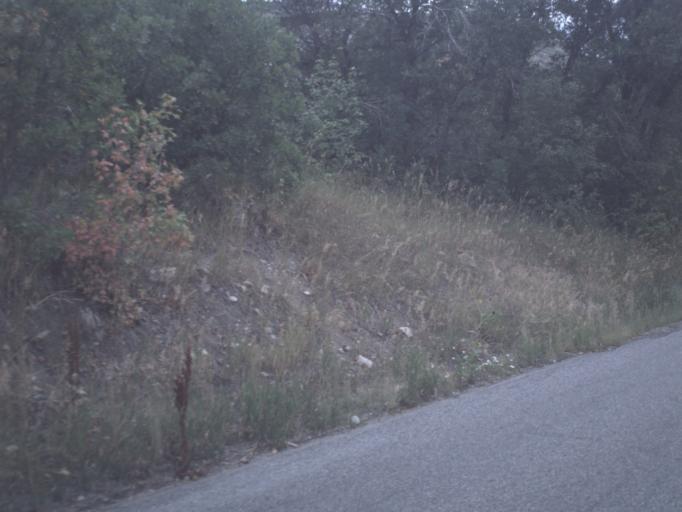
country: US
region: Utah
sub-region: Utah County
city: Lindon
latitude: 40.3960
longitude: -111.5861
